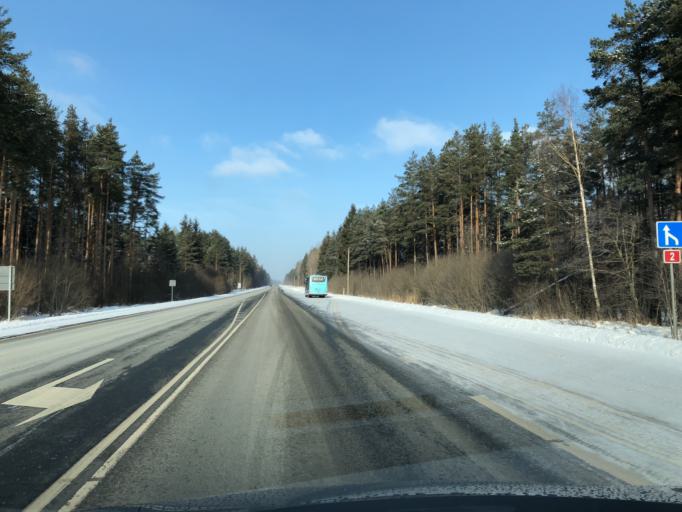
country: EE
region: Tartu
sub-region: Tartu linn
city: Tartu
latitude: 58.3874
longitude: 26.6687
